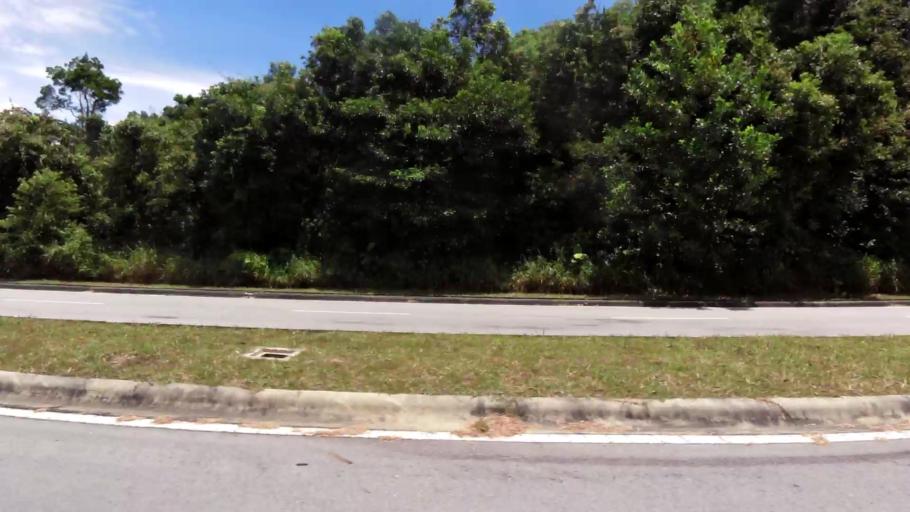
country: BN
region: Brunei and Muara
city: Bandar Seri Begawan
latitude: 4.9445
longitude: 114.8919
